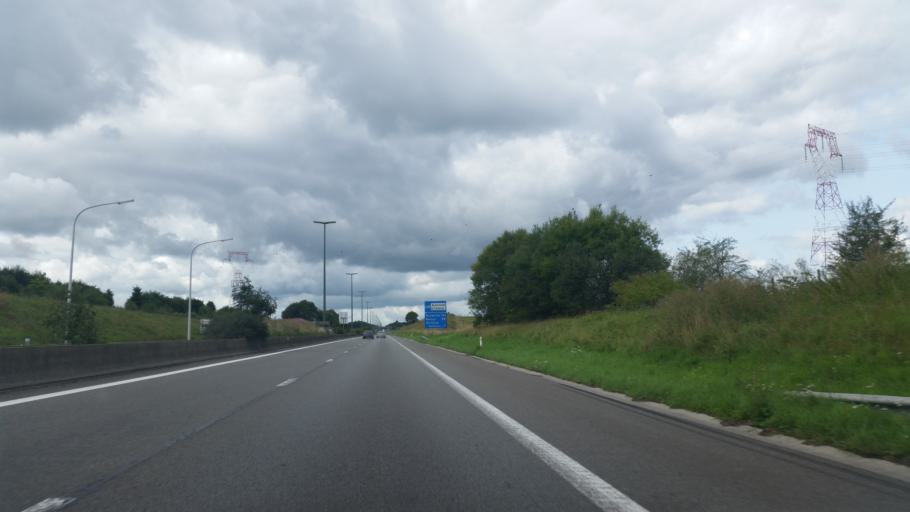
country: BE
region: Wallonia
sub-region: Province du Luxembourg
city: Neufchateau
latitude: 49.8762
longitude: 5.4726
